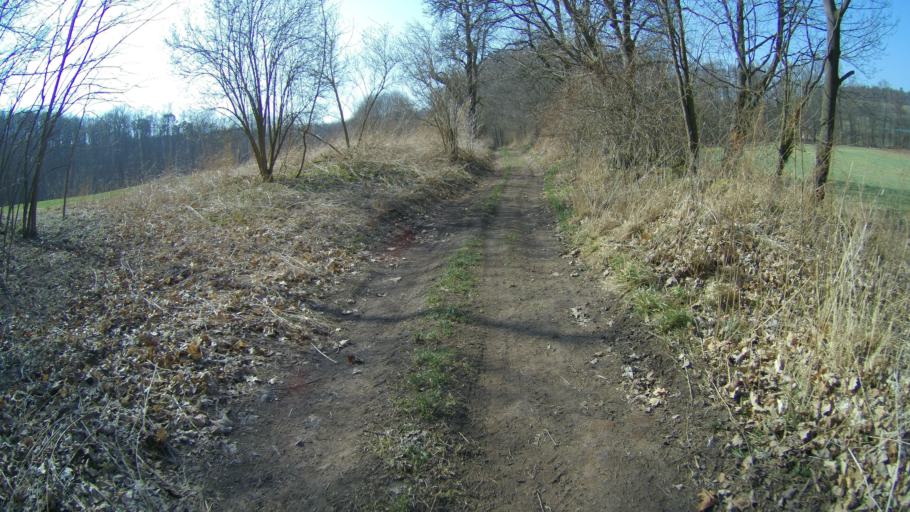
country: CZ
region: Ustecky
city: Mecholupy
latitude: 50.2690
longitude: 13.5575
